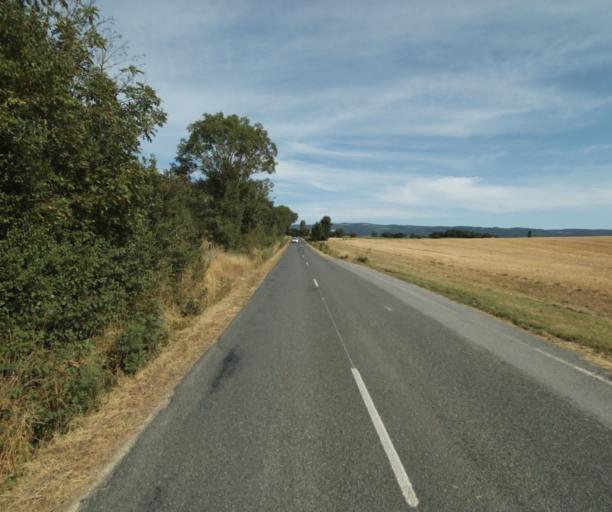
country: FR
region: Midi-Pyrenees
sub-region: Departement du Tarn
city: Soual
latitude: 43.5161
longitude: 2.0783
